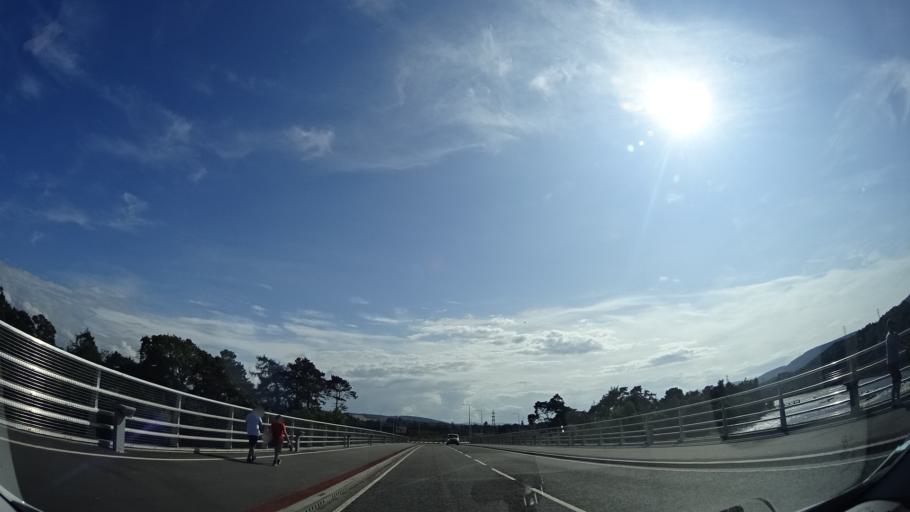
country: GB
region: Scotland
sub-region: Highland
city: Inverness
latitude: 57.4592
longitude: -4.2472
